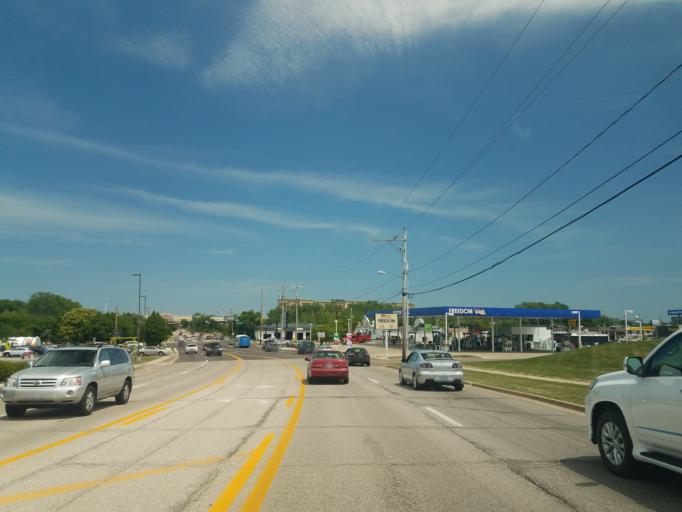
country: US
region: Illinois
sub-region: McLean County
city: Normal
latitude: 40.5012
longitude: -88.9576
